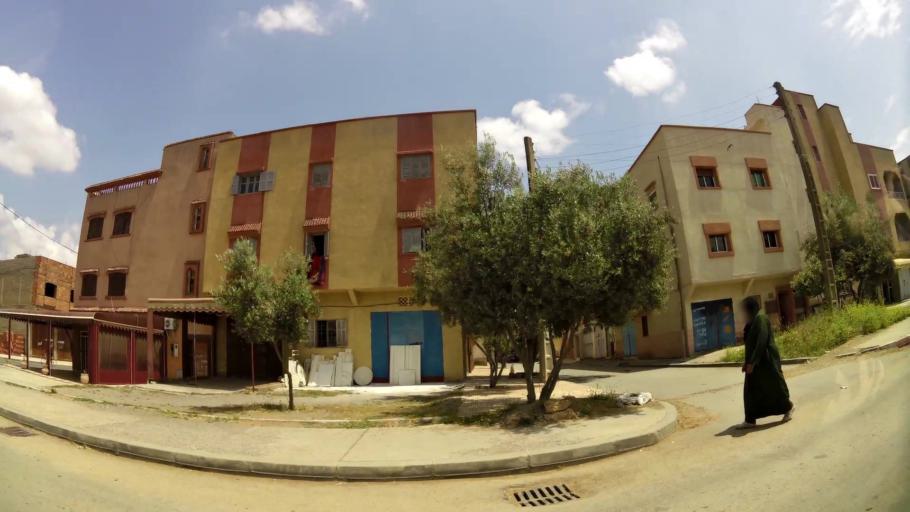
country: MA
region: Rabat-Sale-Zemmour-Zaer
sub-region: Khemisset
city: Tiflet
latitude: 34.0061
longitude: -6.5297
